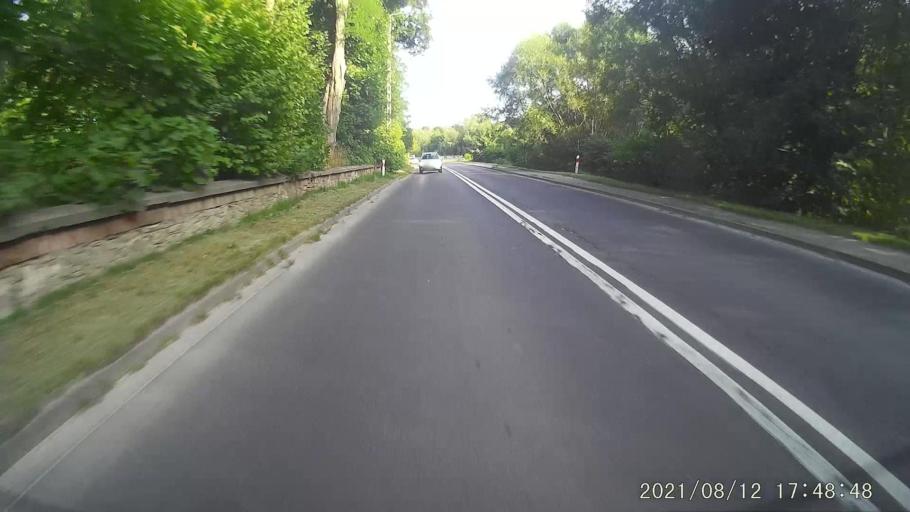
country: PL
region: Lower Silesian Voivodeship
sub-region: Powiat klodzki
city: Bystrzyca Klodzka
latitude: 50.3575
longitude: 16.7248
